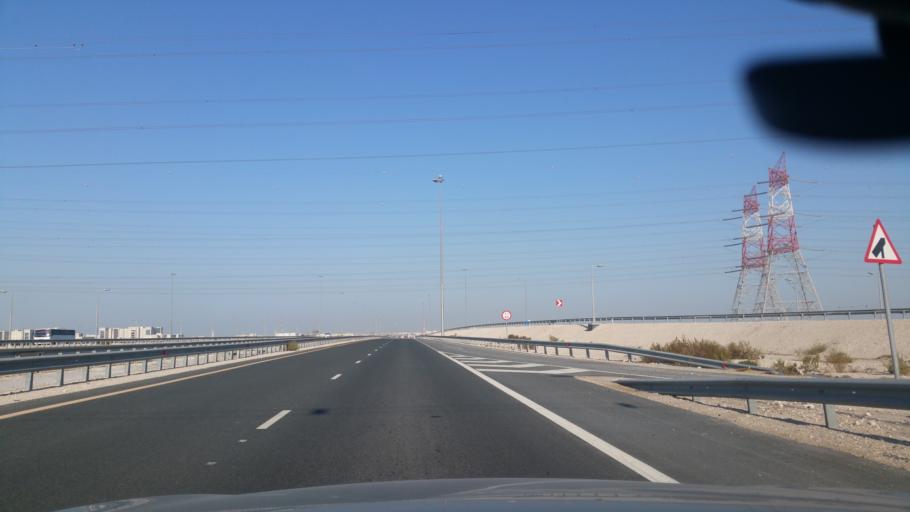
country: QA
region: Baladiyat ar Rayyan
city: Ar Rayyan
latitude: 25.1738
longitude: 51.3314
